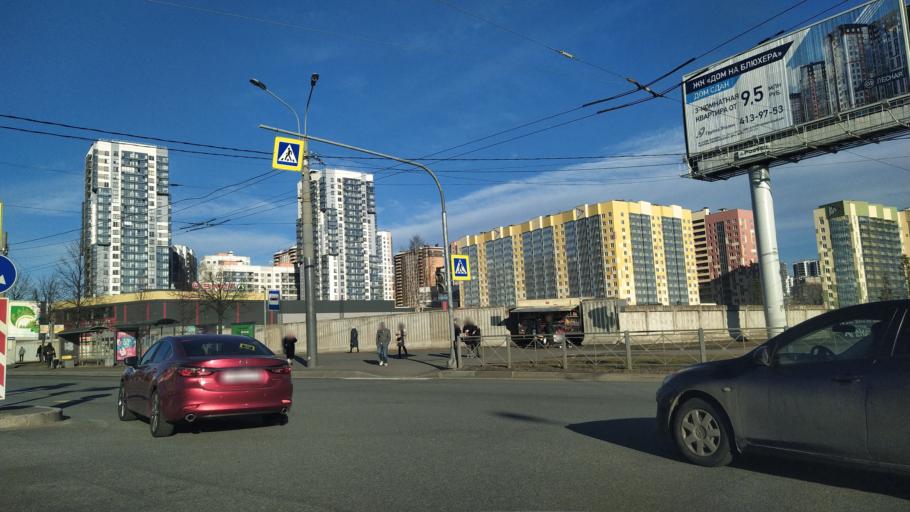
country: RU
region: St.-Petersburg
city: Kushelevka
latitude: 59.9856
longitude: 30.3646
